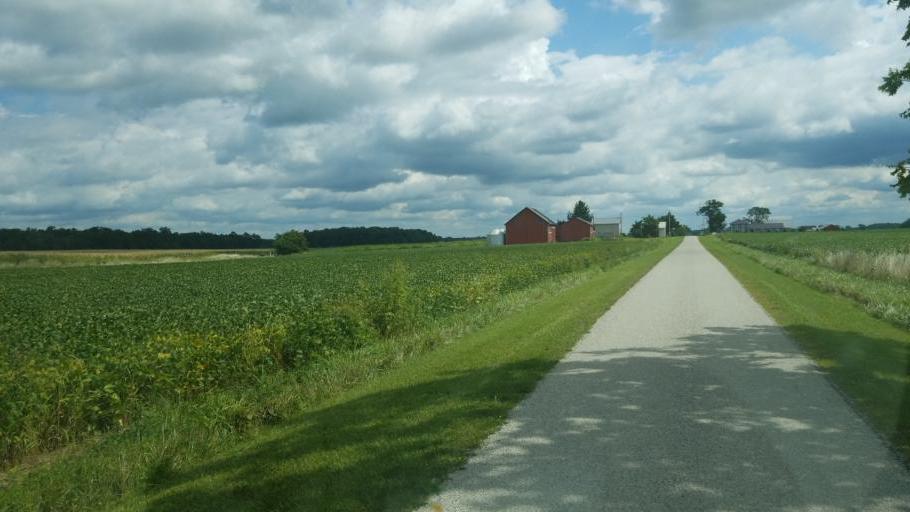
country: US
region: Ohio
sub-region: Huron County
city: Willard
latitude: 41.1160
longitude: -82.8042
